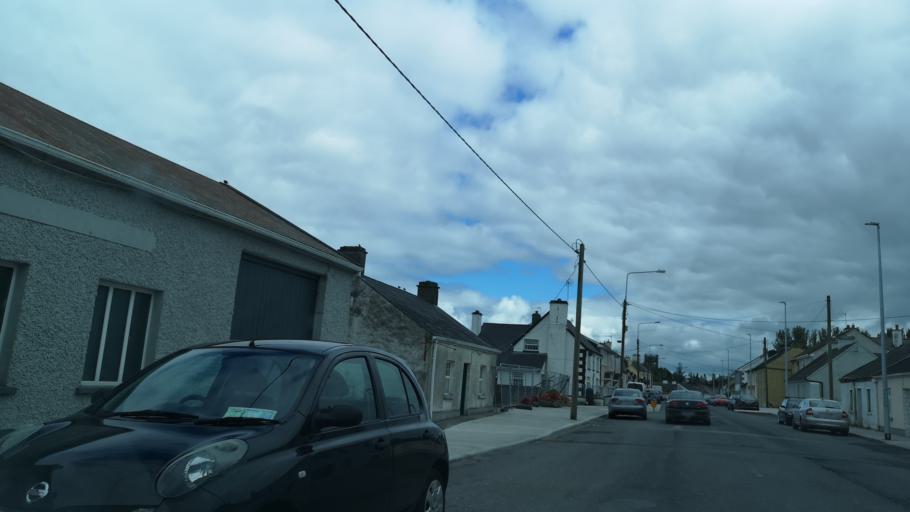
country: IE
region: Leinster
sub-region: Uibh Fhaili
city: Banagher
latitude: 53.2796
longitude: -8.0473
